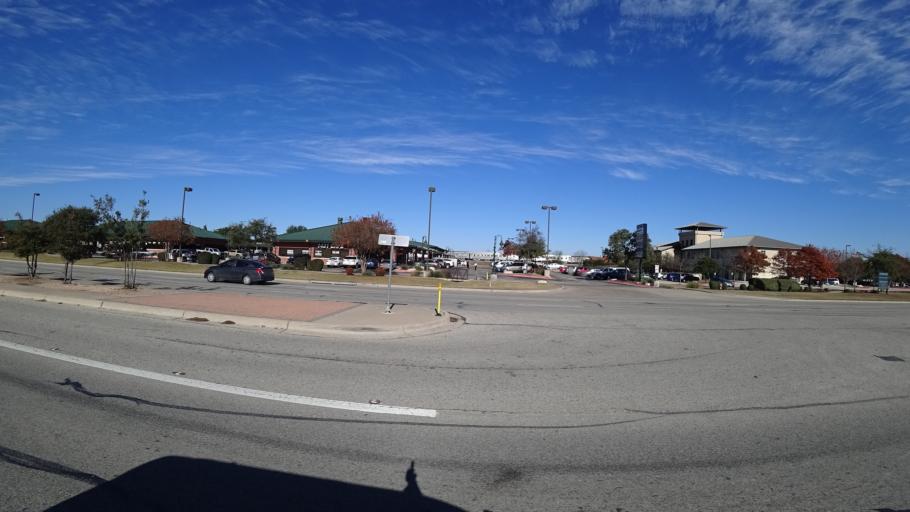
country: US
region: Texas
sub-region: Williamson County
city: Cedar Park
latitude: 30.5230
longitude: -97.8233
